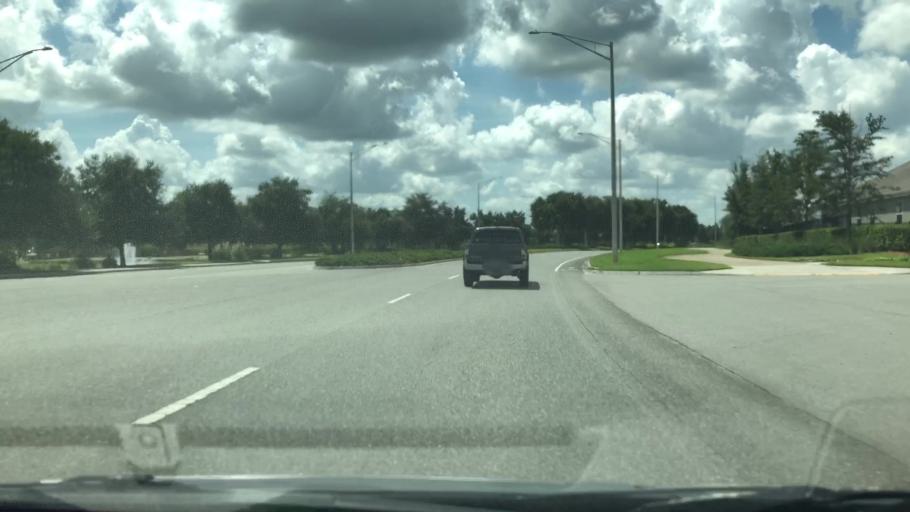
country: US
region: Florida
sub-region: Saint Johns County
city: Fruit Cove
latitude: 30.1130
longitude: -81.5184
